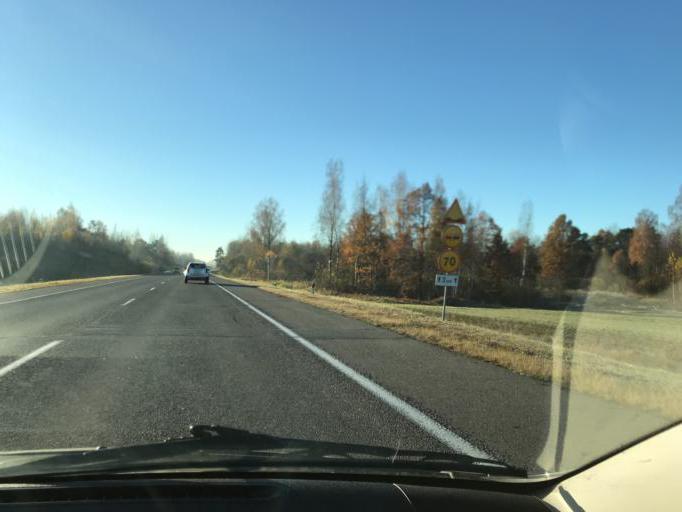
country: BY
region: Vitebsk
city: Vitebsk
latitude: 54.9689
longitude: 30.3522
